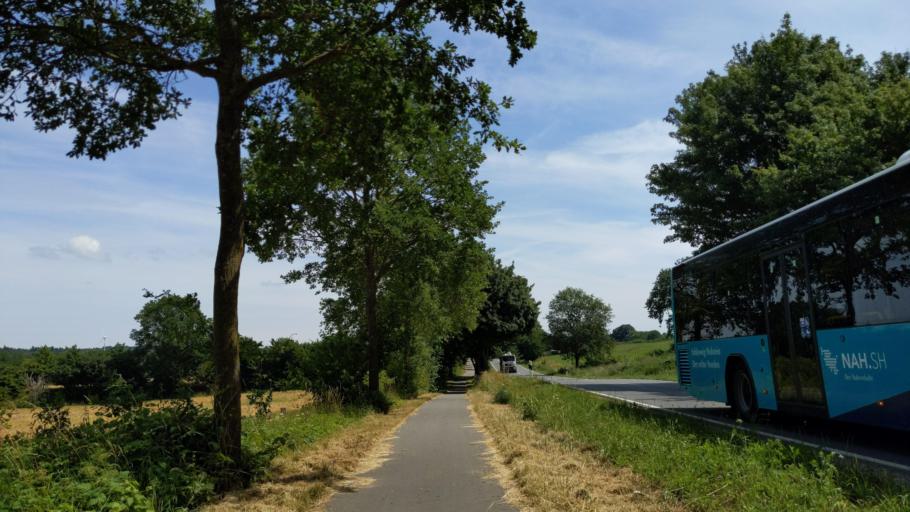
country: DE
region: Schleswig-Holstein
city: Bosdorf
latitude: 54.1490
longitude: 10.5060
